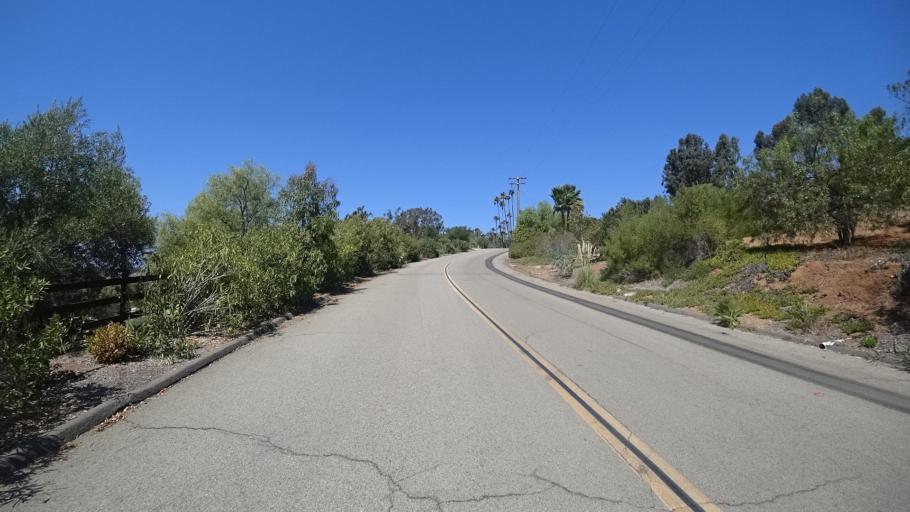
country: US
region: California
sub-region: San Diego County
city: Fairbanks Ranch
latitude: 33.0128
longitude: -117.1776
